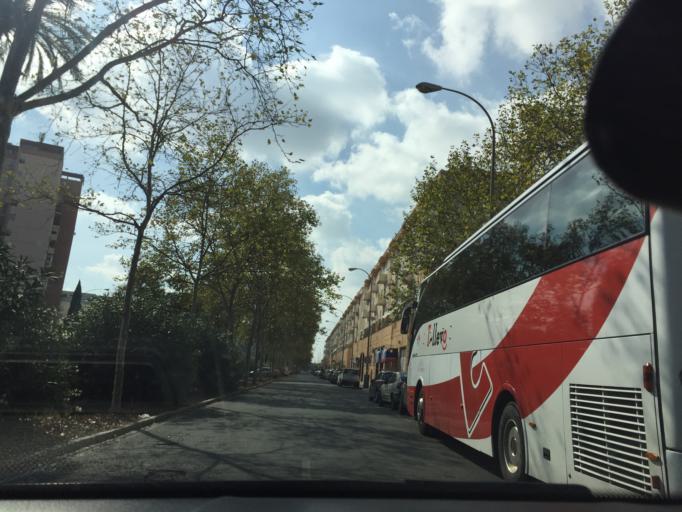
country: ES
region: Andalusia
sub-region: Provincia de Sevilla
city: Sevilla
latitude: 37.3966
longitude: -5.9671
